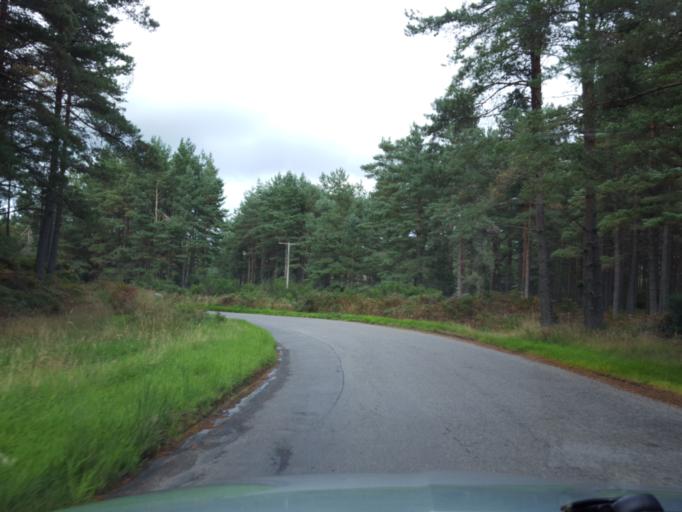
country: GB
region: Scotland
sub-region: Aberdeenshire
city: Banchory
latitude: 56.9983
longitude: -2.5786
